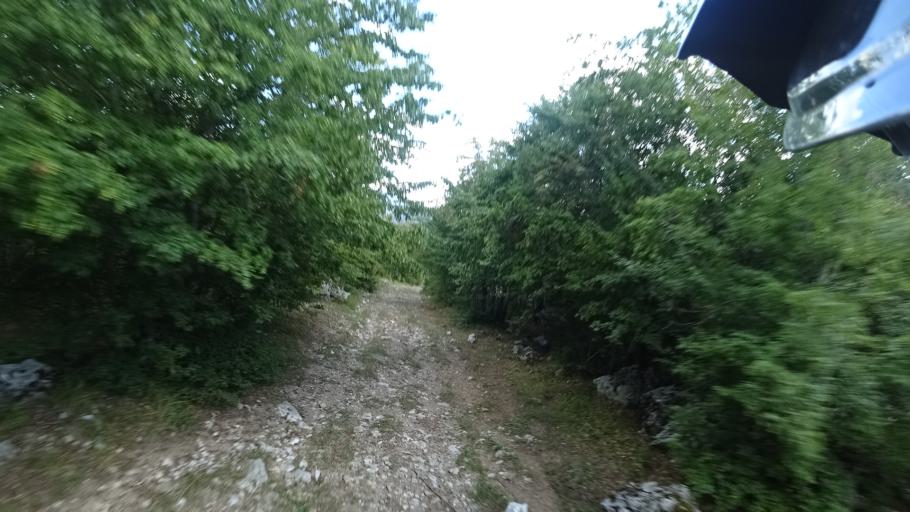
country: HR
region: Zadarska
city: Gracac
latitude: 44.3664
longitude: 16.0884
